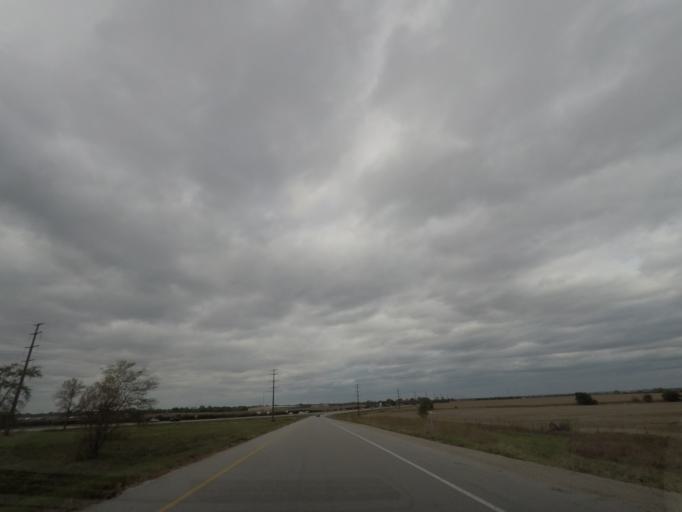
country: US
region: Iowa
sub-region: Story County
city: Huxley
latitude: 41.8786
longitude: -93.5694
